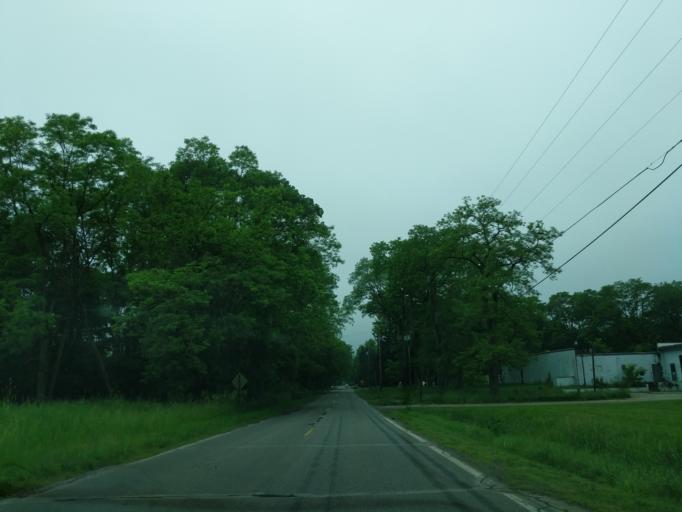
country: US
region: Michigan
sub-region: Jackson County
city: Spring Arbor
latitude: 42.2183
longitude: -84.5558
